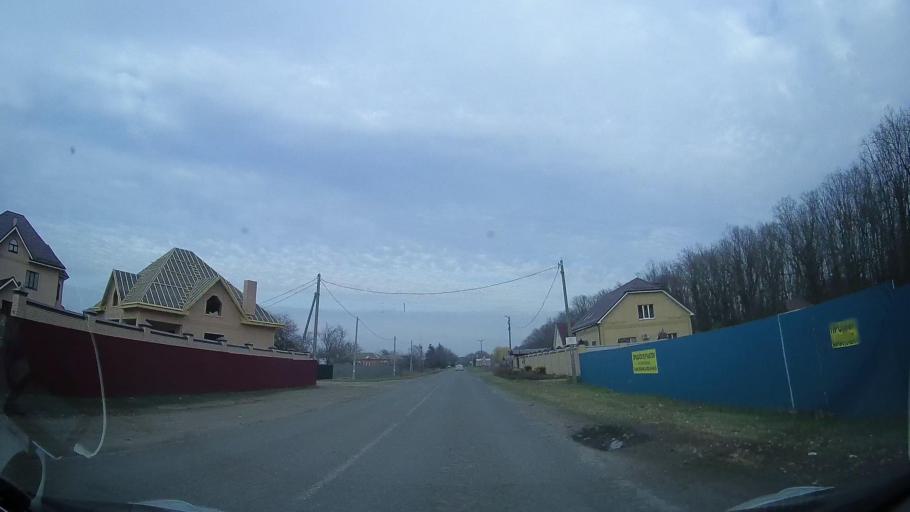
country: RU
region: Rostov
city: Ol'ginskaya
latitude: 47.1303
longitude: 39.8823
